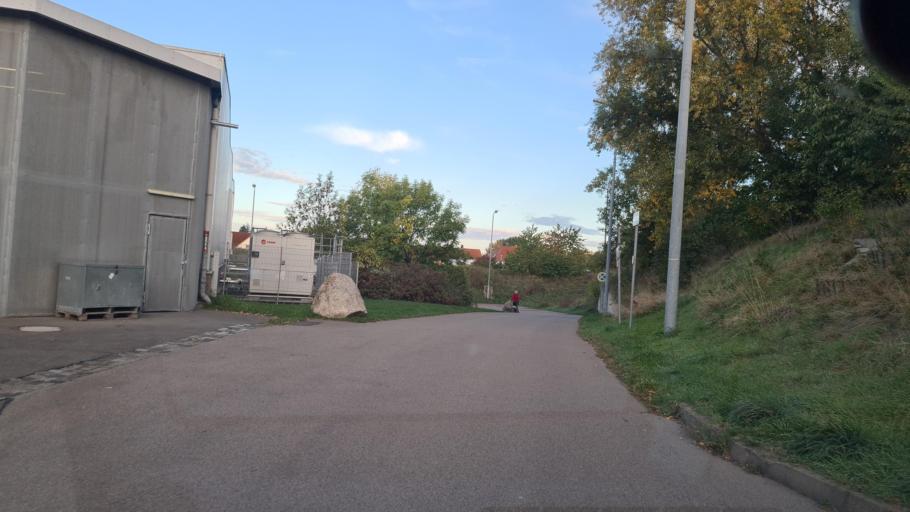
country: DE
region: Saxony
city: Grossposna
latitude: 51.2699
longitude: 12.4979
